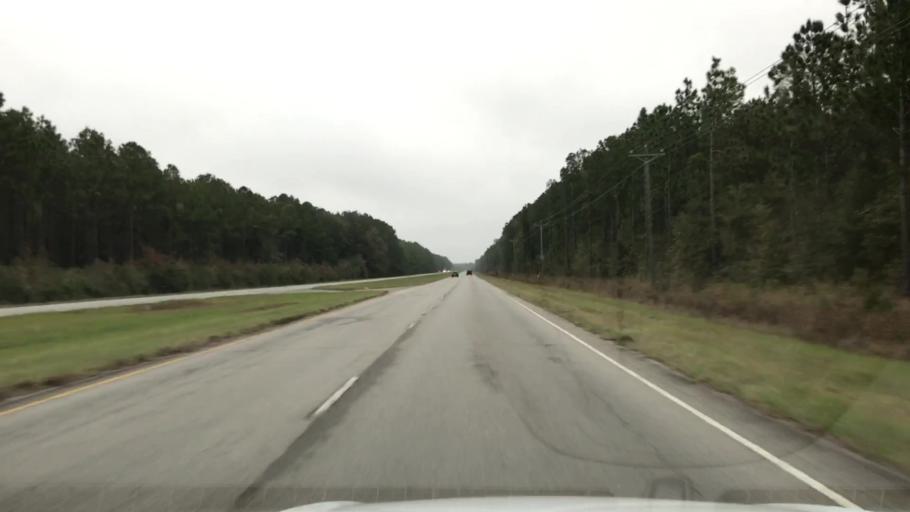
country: US
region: South Carolina
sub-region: Charleston County
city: Awendaw
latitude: 33.0114
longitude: -79.6378
